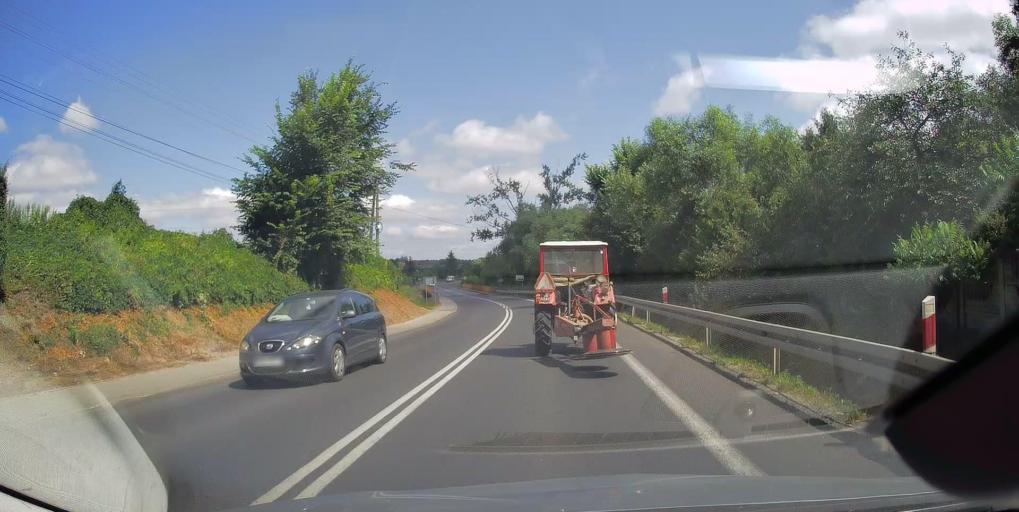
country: PL
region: Subcarpathian Voivodeship
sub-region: Powiat debicki
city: Brzeznica
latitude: 50.1056
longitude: 21.4865
